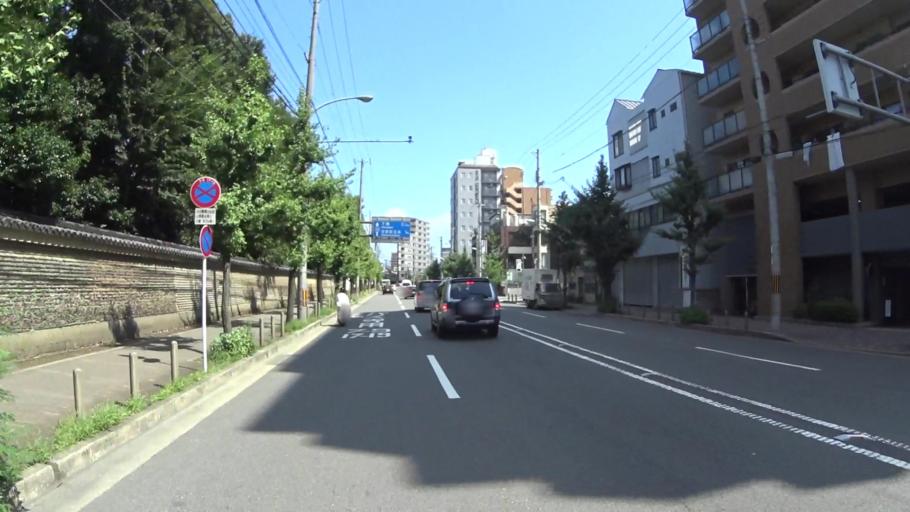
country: JP
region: Kyoto
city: Kyoto
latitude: 34.9903
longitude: 135.7641
